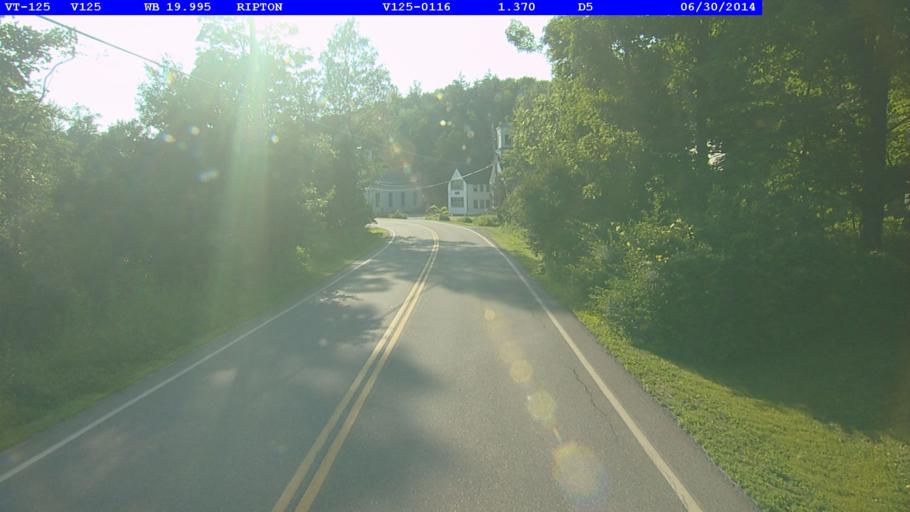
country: US
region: Vermont
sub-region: Addison County
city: Middlebury (village)
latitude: 43.9746
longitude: -73.0354
